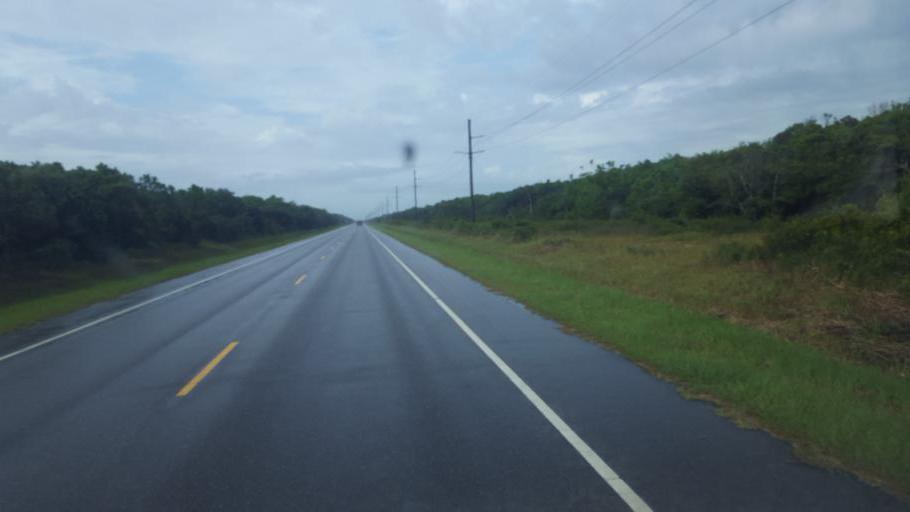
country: US
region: North Carolina
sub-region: Dare County
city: Buxton
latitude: 35.5194
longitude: -75.4759
